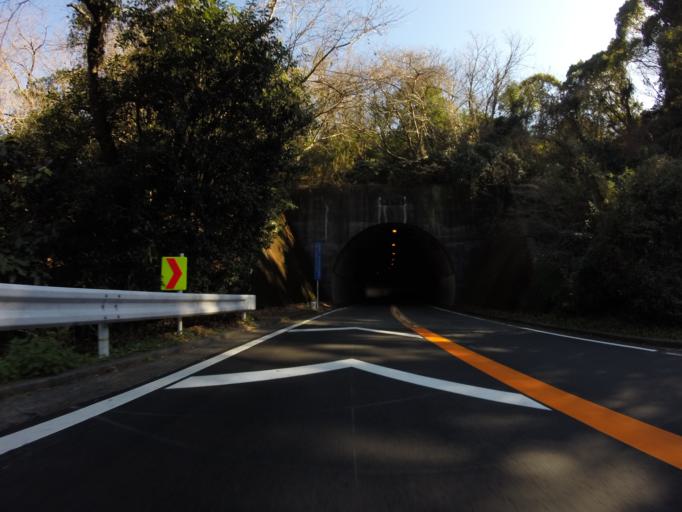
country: JP
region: Shizuoka
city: Shizuoka-shi
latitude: 34.9768
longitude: 138.4850
